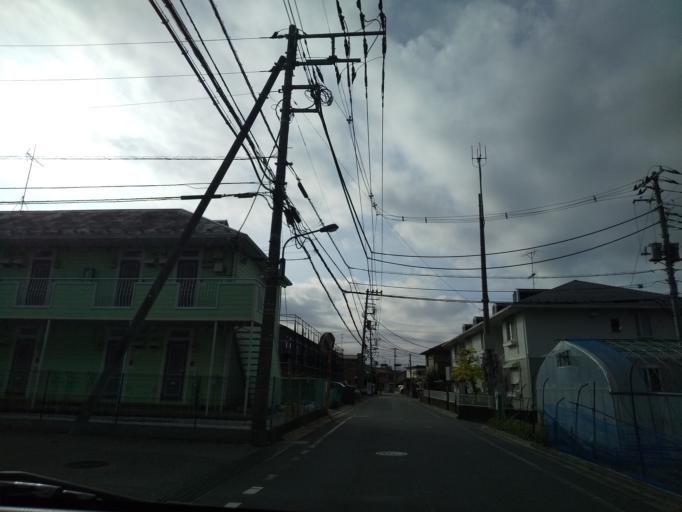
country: JP
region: Tokyo
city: Hachioji
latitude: 35.6797
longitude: 139.3217
